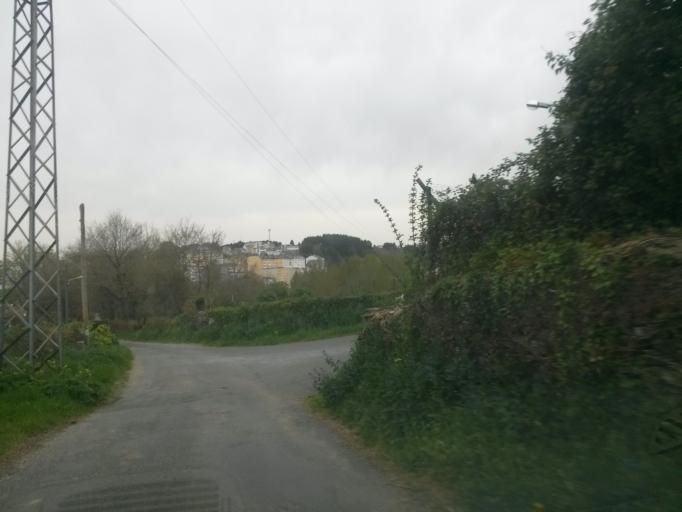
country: ES
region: Galicia
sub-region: Provincia de Lugo
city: Lugo
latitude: 43.0129
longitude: -7.5437
